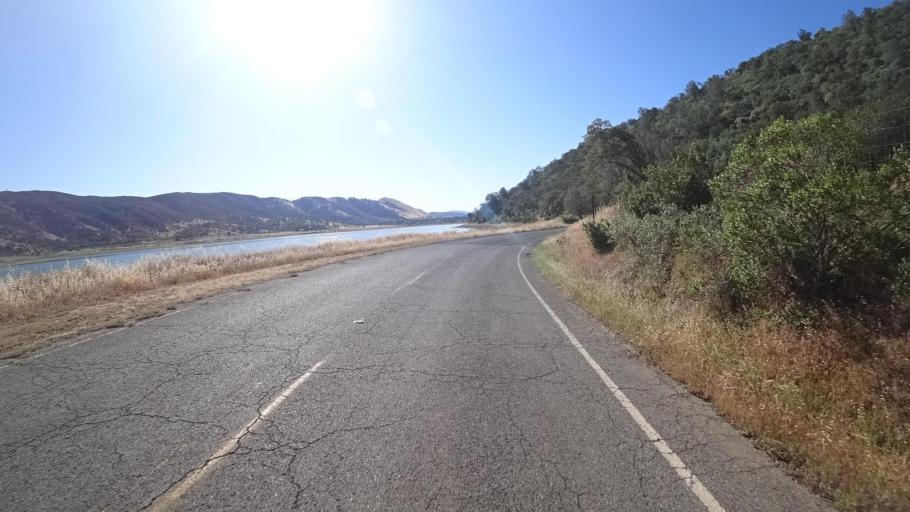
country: US
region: California
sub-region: Lake County
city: Clearlake Oaks
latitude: 38.9878
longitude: -122.6825
